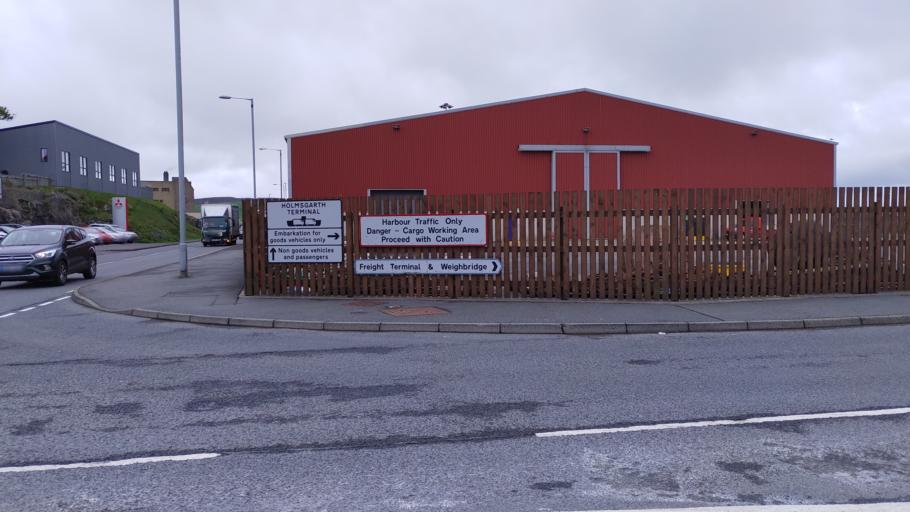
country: GB
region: Scotland
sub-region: Shetland Islands
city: Lerwick
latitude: 60.1600
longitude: -1.1571
